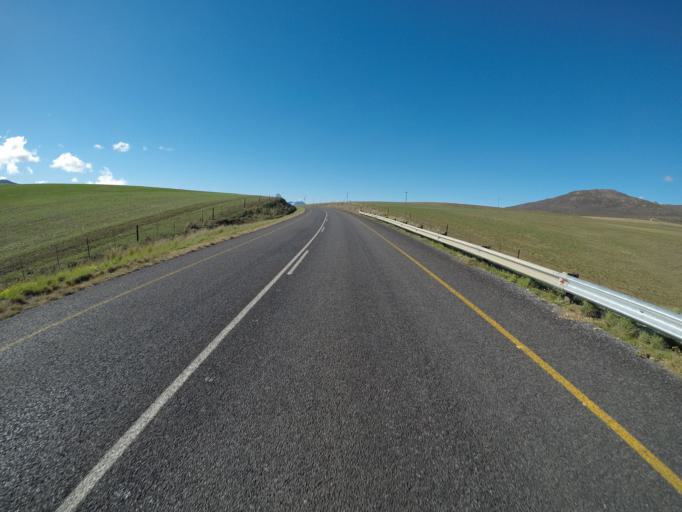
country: ZA
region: Western Cape
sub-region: Overberg District Municipality
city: Caledon
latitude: -34.1552
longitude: 19.4690
